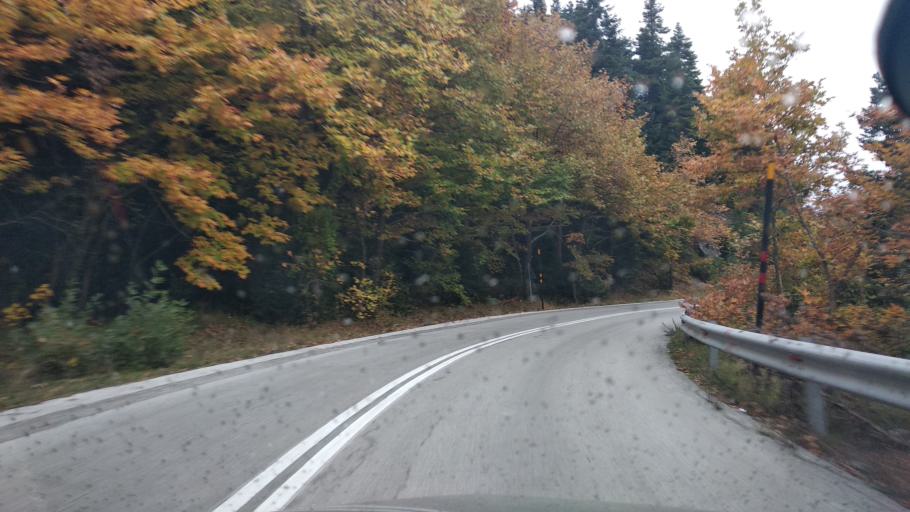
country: GR
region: Thessaly
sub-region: Trikala
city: Pyli
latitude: 39.5264
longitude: 21.5173
